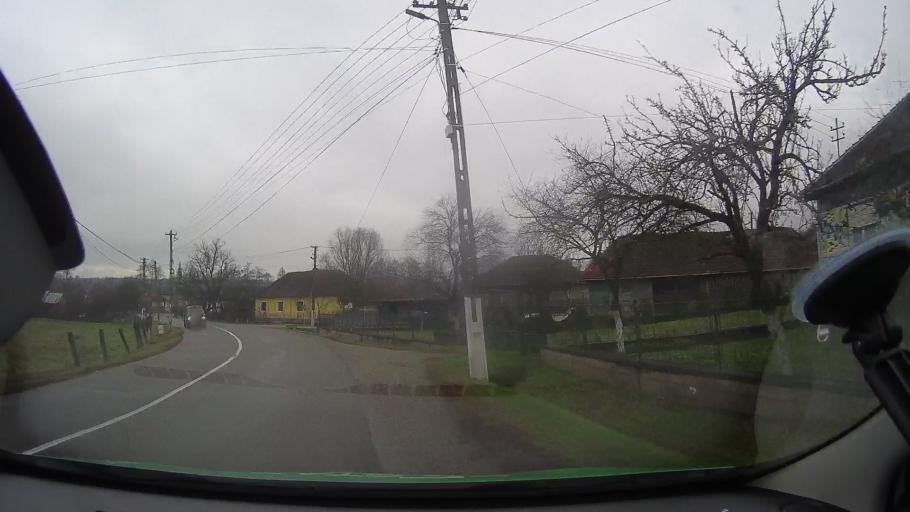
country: RO
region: Arad
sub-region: Comuna Varfurile
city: Varfurile
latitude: 46.3112
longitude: 22.5174
